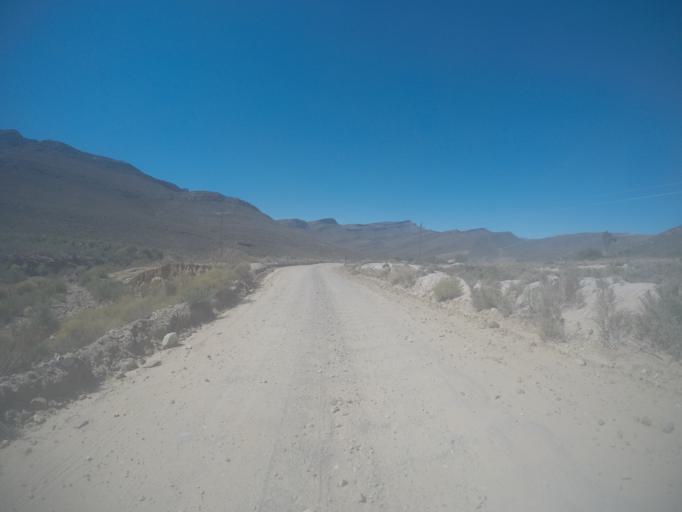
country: ZA
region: Western Cape
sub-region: West Coast District Municipality
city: Clanwilliam
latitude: -32.5485
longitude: 19.3600
